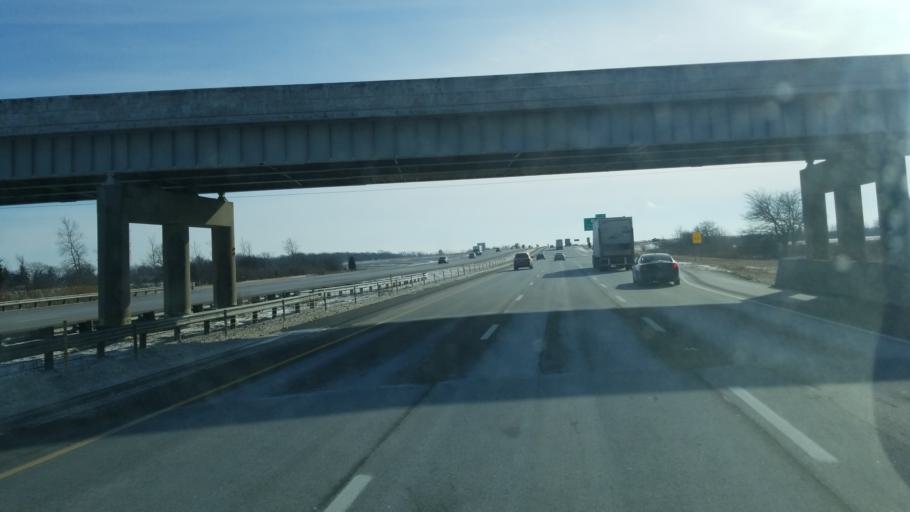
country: US
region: Ohio
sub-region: Wood County
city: Bowling Green
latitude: 41.3566
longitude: -83.6215
